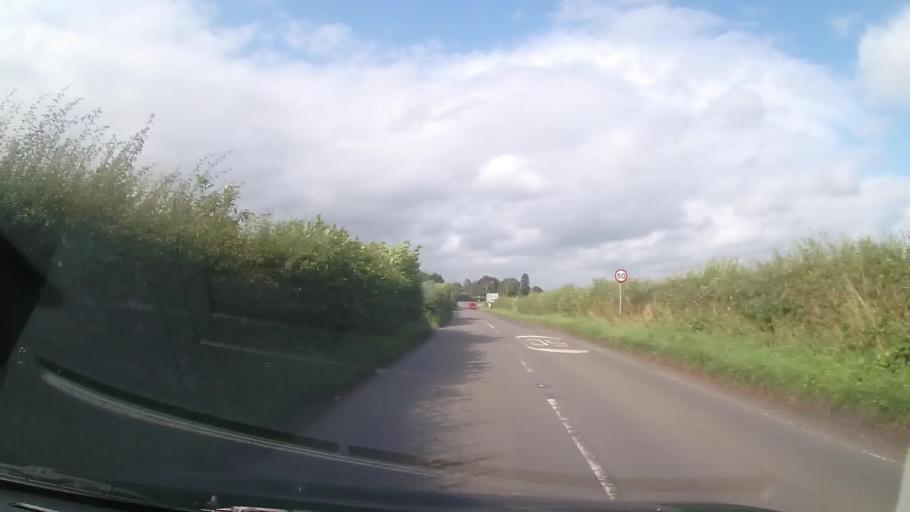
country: GB
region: England
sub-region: Shropshire
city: Bishop's Castle
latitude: 52.4942
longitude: -2.9893
